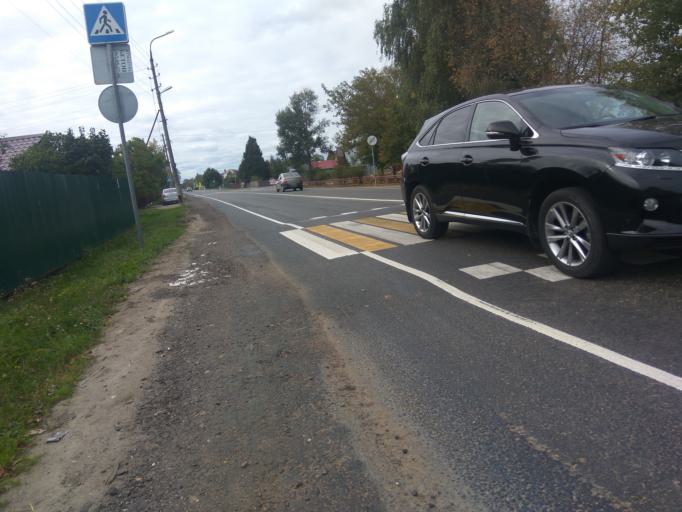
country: RU
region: Moskovskaya
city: Chernogolovka
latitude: 56.0642
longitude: 38.2609
